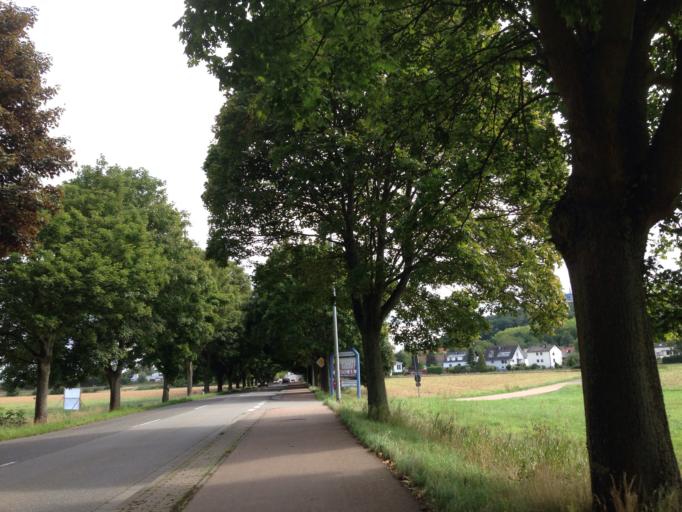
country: DE
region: Hesse
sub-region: Regierungsbezirk Giessen
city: Limburg an der Lahn
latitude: 50.3928
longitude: 8.0423
